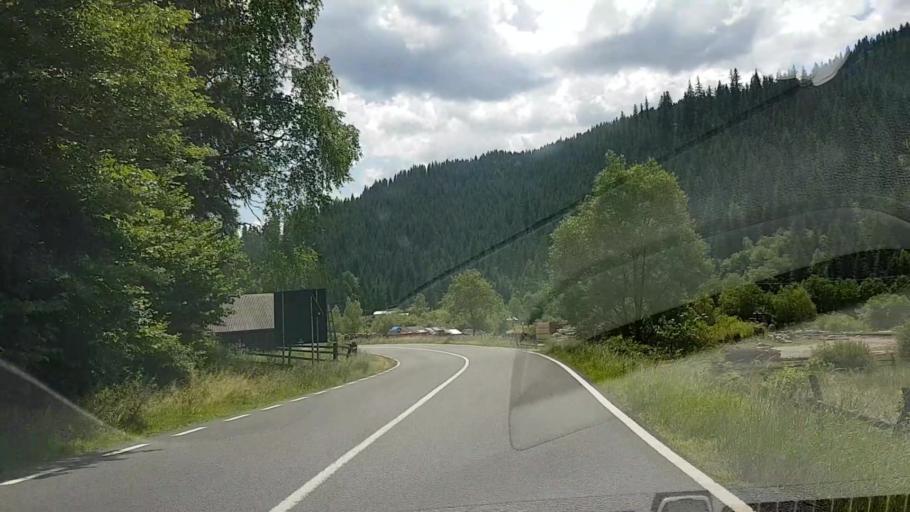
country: RO
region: Suceava
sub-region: Comuna Crucea
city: Crucea
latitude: 47.3959
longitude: 25.5637
